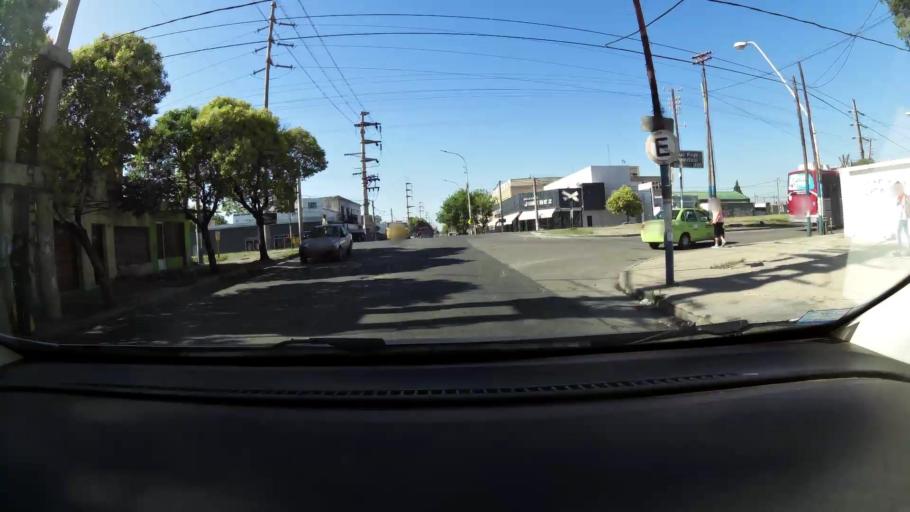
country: AR
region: Cordoba
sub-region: Departamento de Capital
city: Cordoba
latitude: -31.4403
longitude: -64.1688
